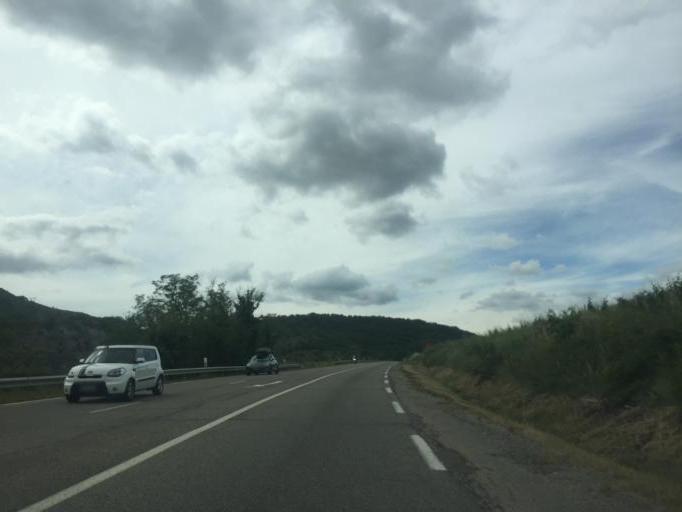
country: FR
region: Rhone-Alpes
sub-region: Departement de l'Ardeche
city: Alba-la-Romaine
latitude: 44.5726
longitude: 4.5829
